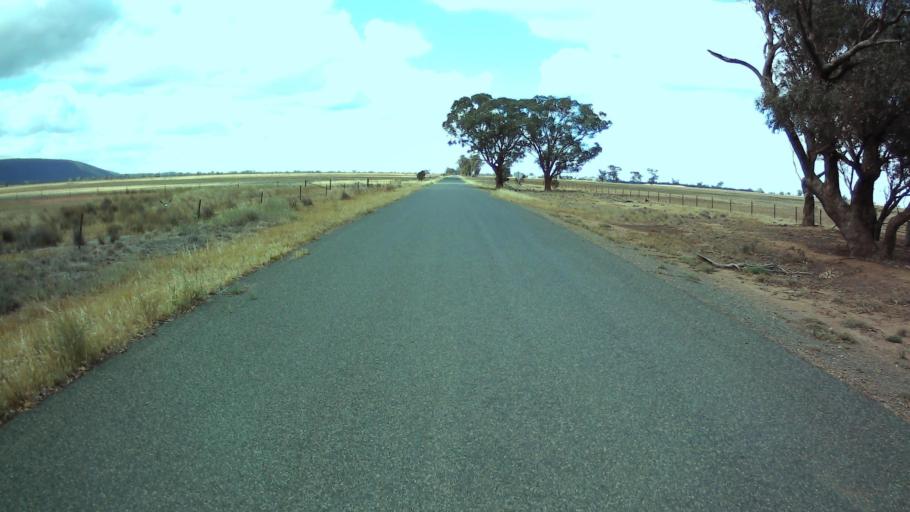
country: AU
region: New South Wales
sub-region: Weddin
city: Grenfell
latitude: -33.8673
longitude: 147.9271
